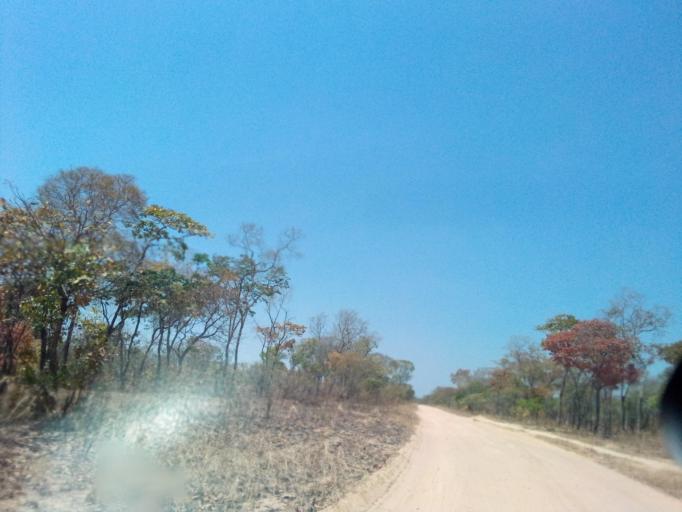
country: ZM
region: Northern
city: Mpika
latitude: -12.2342
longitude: 30.6583
